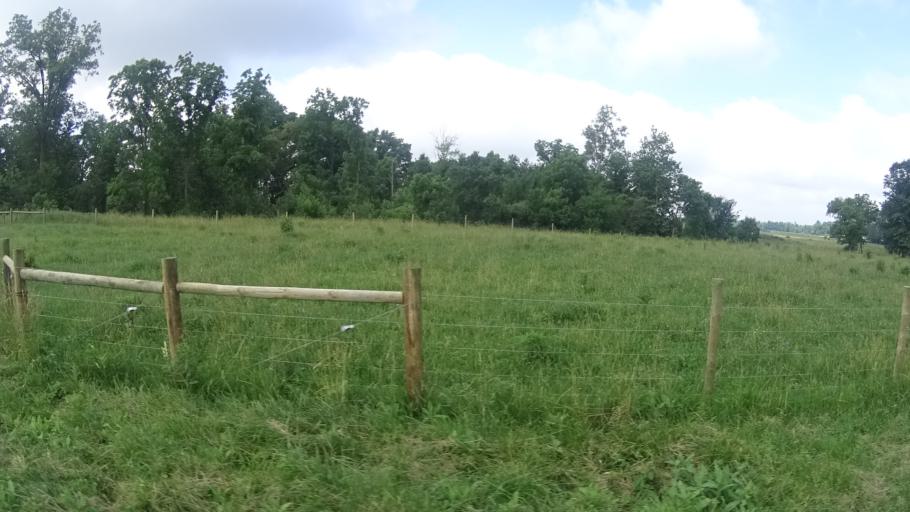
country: US
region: Ohio
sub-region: Huron County
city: Wakeman
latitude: 41.3001
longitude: -82.4583
